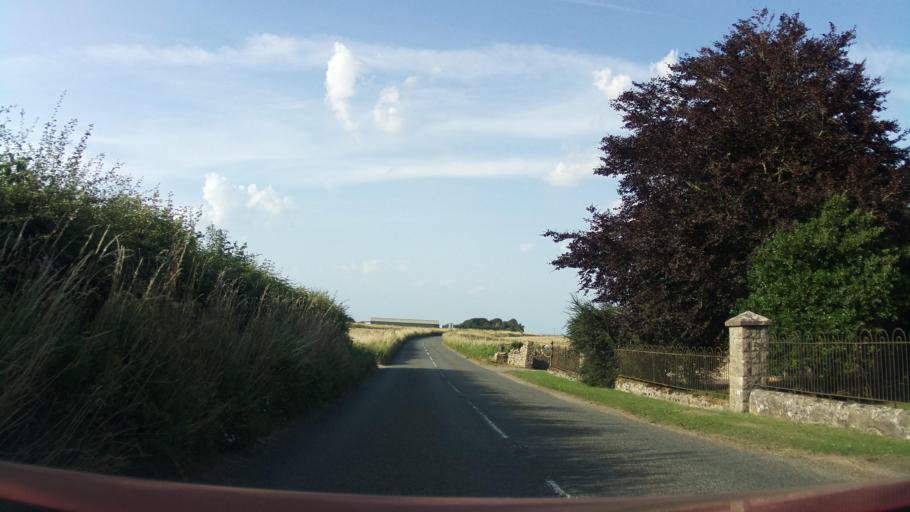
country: GB
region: England
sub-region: South Gloucestershire
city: Marshfield
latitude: 51.4660
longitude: -2.3163
